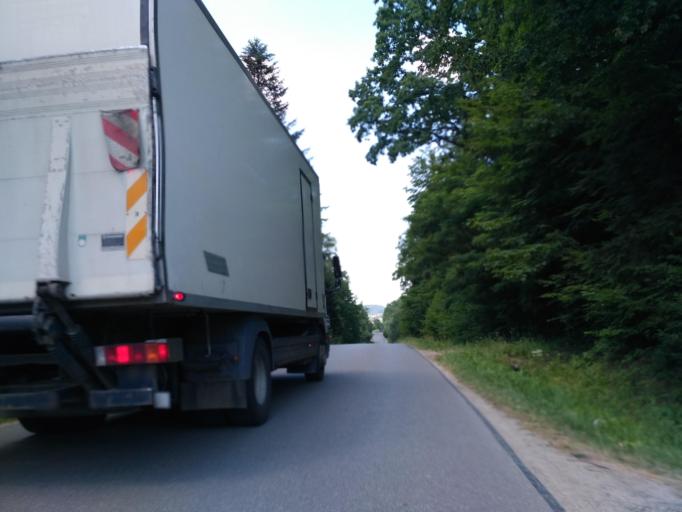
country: PL
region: Subcarpathian Voivodeship
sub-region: Powiat sanocki
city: Niebieszczany
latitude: 49.4891
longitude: 22.1858
